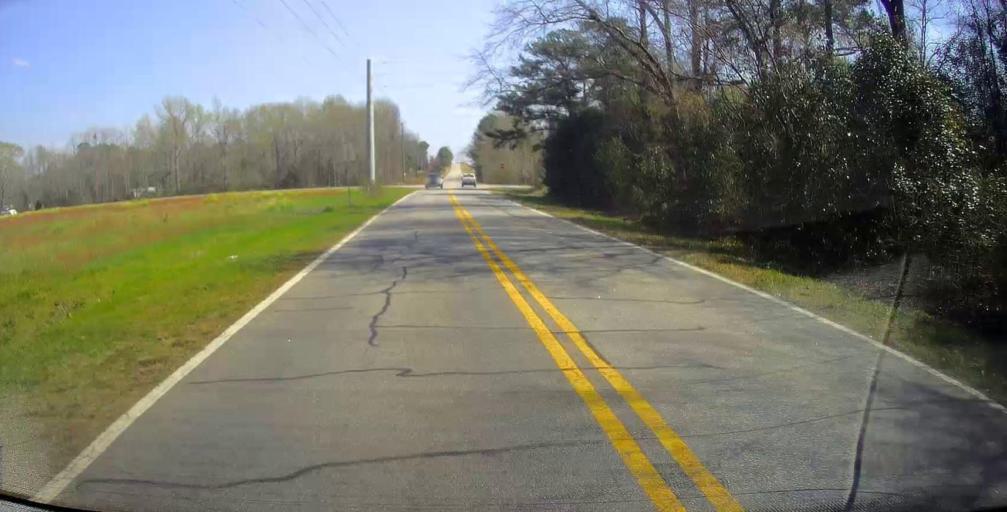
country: US
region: Georgia
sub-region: Peach County
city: Byron
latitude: 32.5784
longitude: -83.7510
